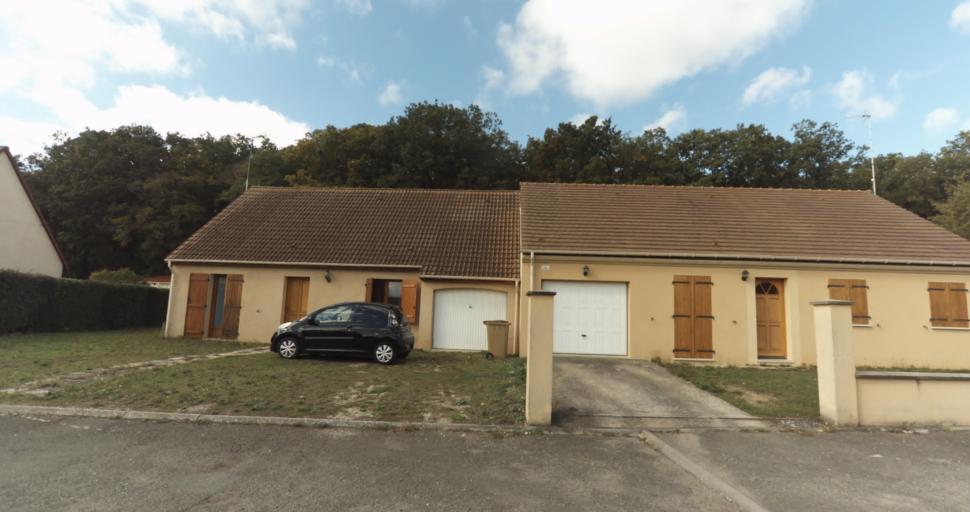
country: FR
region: Centre
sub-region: Departement d'Eure-et-Loir
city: Garnay
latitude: 48.7250
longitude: 1.3235
